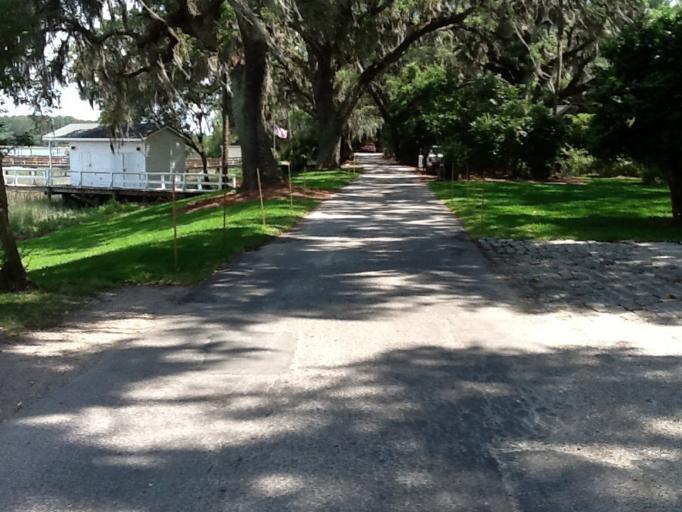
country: US
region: Georgia
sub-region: Chatham County
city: Isle of Hope
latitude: 31.9779
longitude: -81.0565
